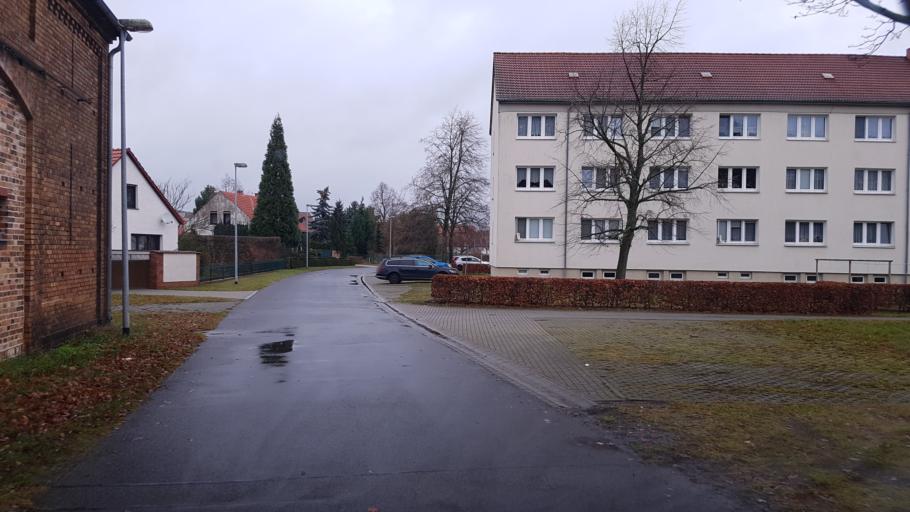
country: DE
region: Brandenburg
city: Altdobern
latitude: 51.6910
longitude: 14.0045
